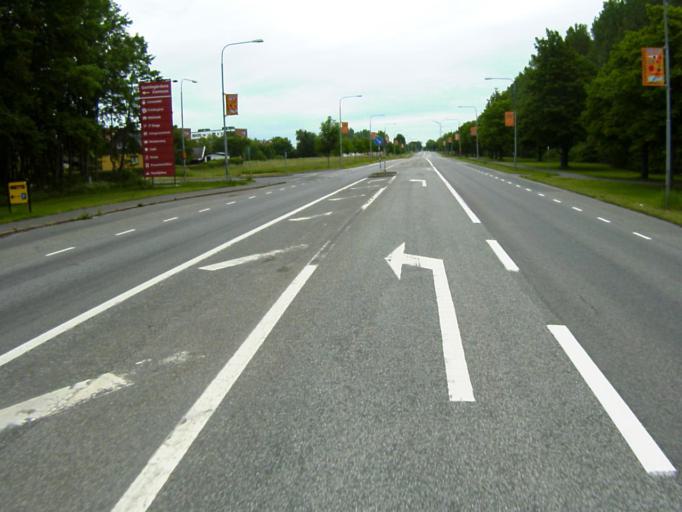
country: SE
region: Skane
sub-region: Kristianstads Kommun
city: Kristianstad
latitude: 56.0553
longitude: 14.1630
